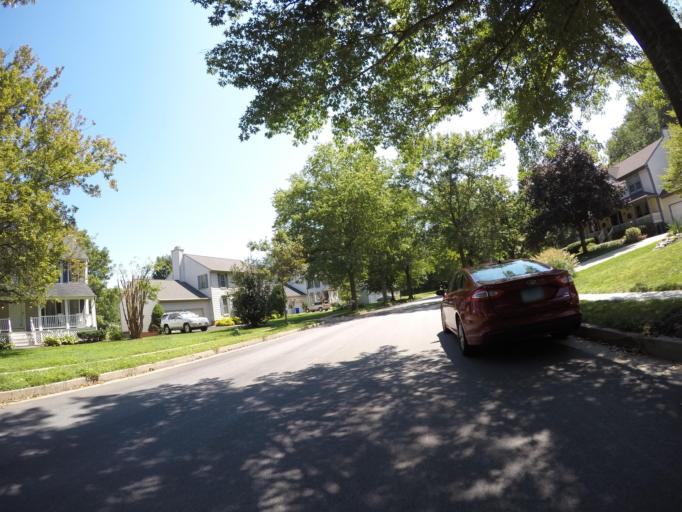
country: US
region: Maryland
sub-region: Howard County
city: Columbia
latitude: 39.2888
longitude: -76.8736
